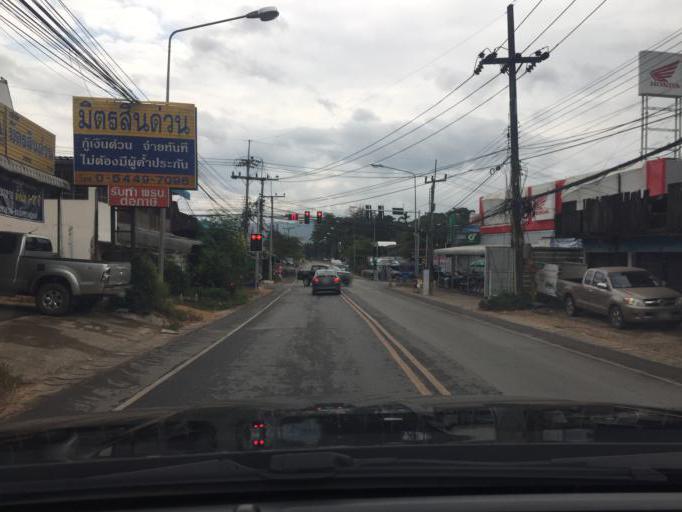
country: TH
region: Phayao
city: Pong
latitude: 19.1707
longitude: 100.2828
